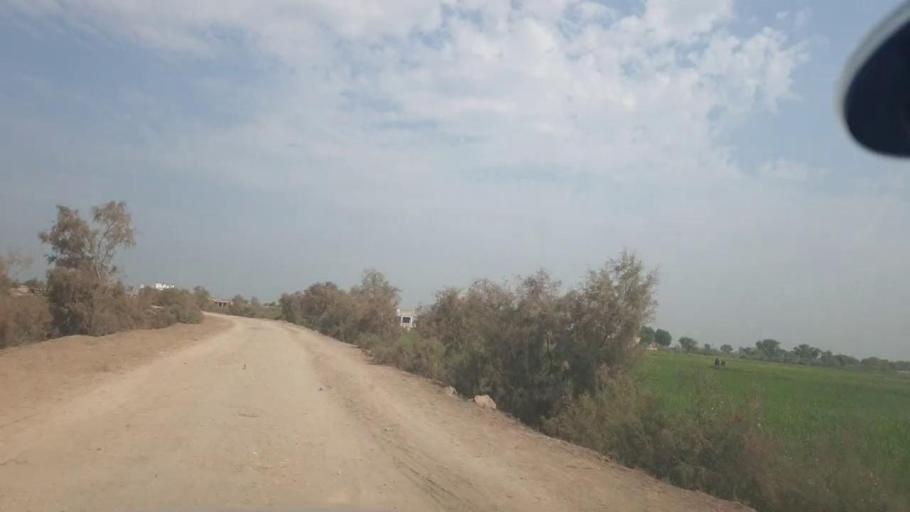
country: PK
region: Balochistan
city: Mehrabpur
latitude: 28.1268
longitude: 68.0890
